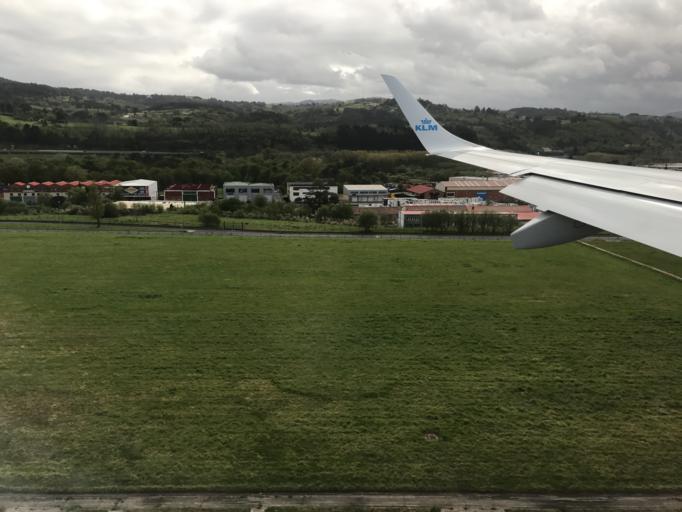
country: ES
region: Basque Country
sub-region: Bizkaia
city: Derio
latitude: 43.2973
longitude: -2.9007
